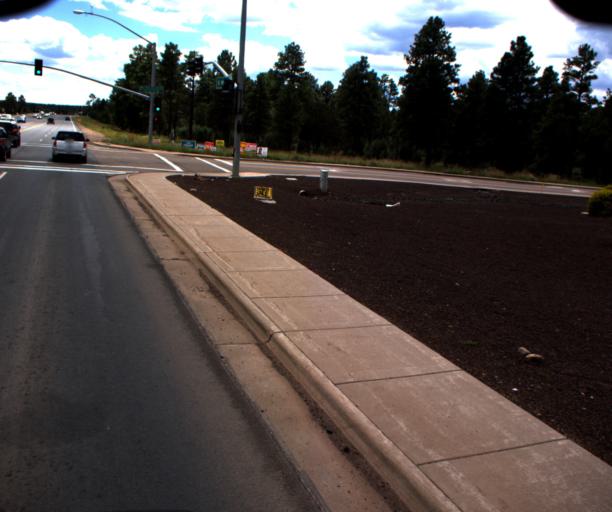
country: US
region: Arizona
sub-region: Navajo County
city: Lake of the Woods
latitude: 34.2023
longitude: -110.0194
